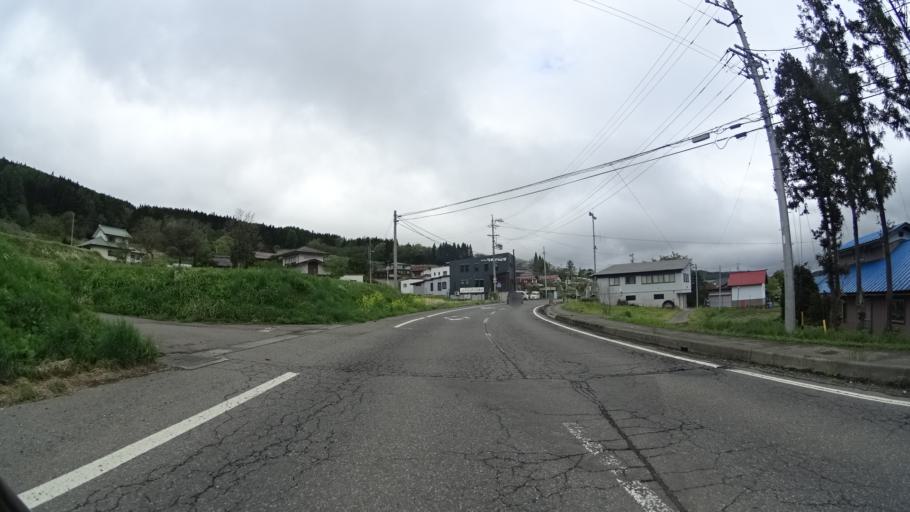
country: JP
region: Nagano
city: Nagano-shi
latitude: 36.7380
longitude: 138.2053
